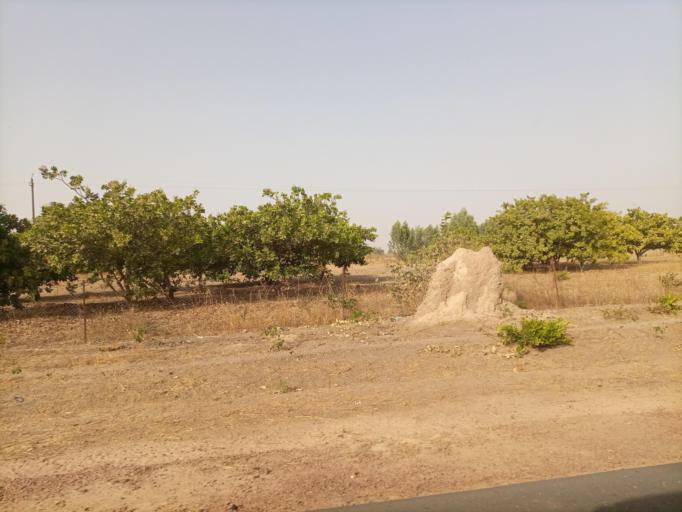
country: SN
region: Fatick
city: Passi
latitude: 14.0176
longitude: -16.2926
